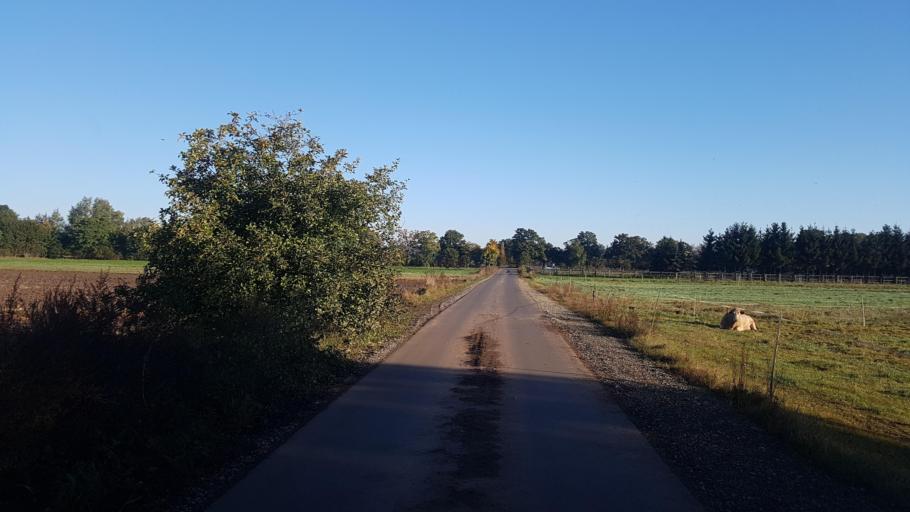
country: DE
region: Brandenburg
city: Hohenleipisch
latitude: 51.4671
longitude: 13.5630
